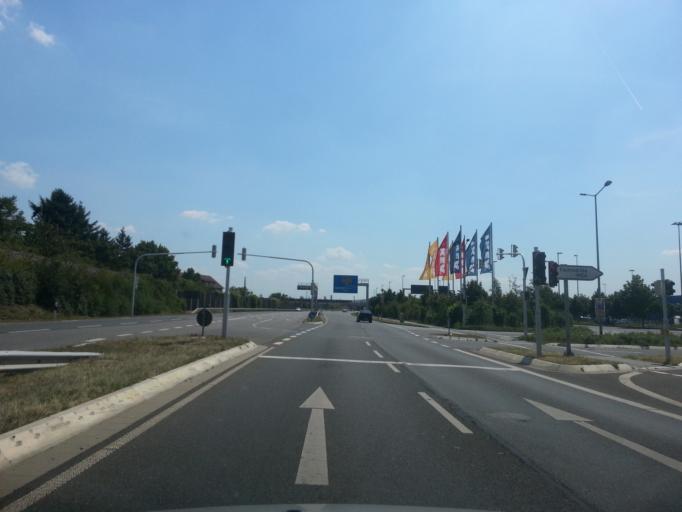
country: DE
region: Hesse
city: Lampertheim
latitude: 49.5580
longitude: 8.4454
